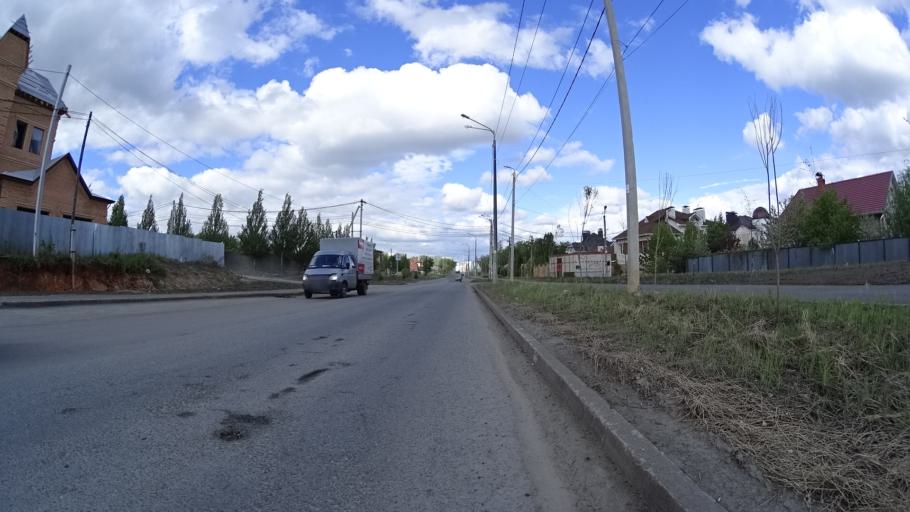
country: RU
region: Chelyabinsk
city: Sargazy
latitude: 55.1530
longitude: 61.2758
